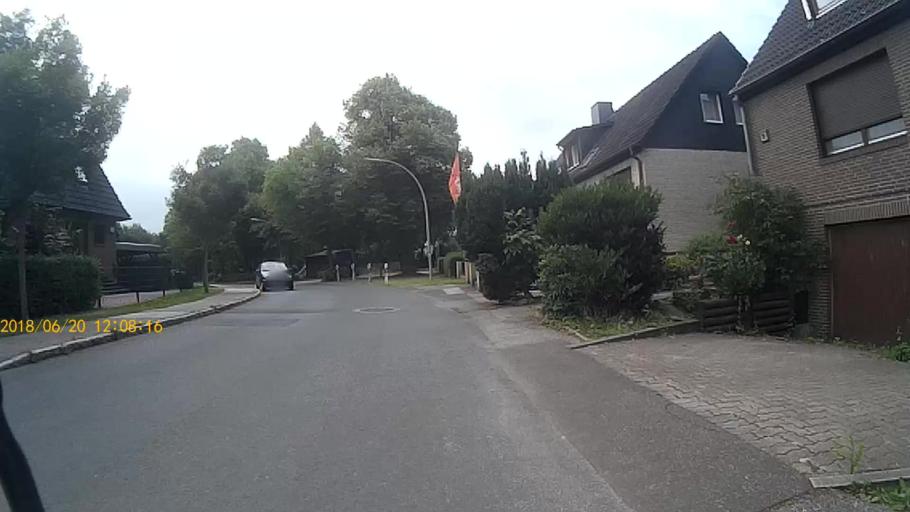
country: DE
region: Hamburg
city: Harburg
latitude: 53.4853
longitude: 10.0074
